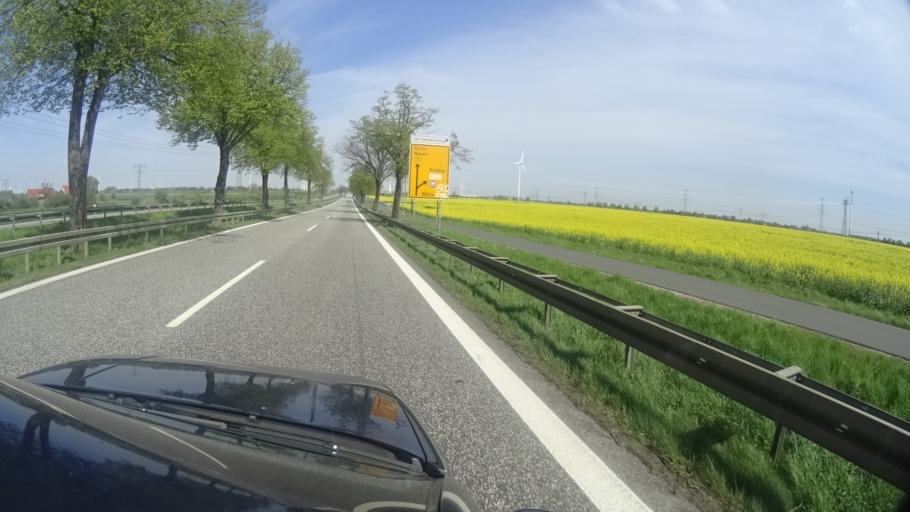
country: DE
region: Brandenburg
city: Wustermark
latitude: 52.5723
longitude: 12.9137
